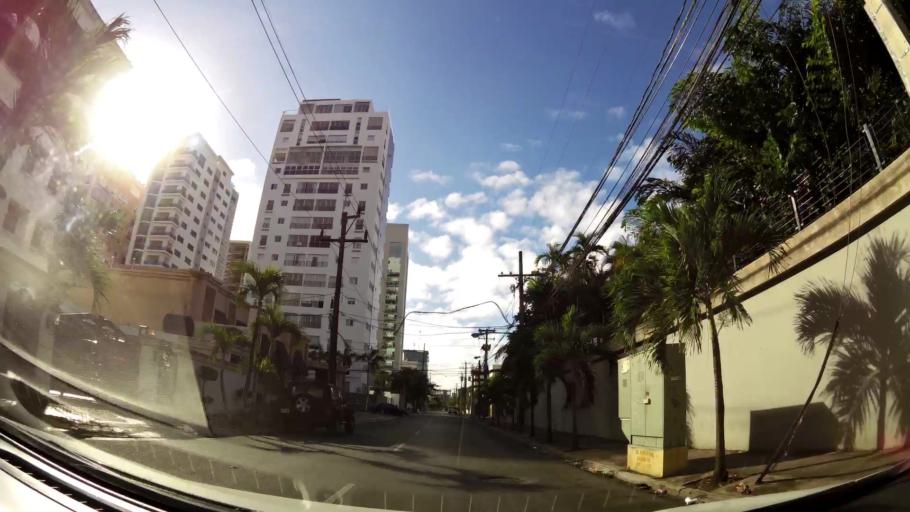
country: DO
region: Nacional
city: La Julia
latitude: 18.4693
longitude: -69.9374
